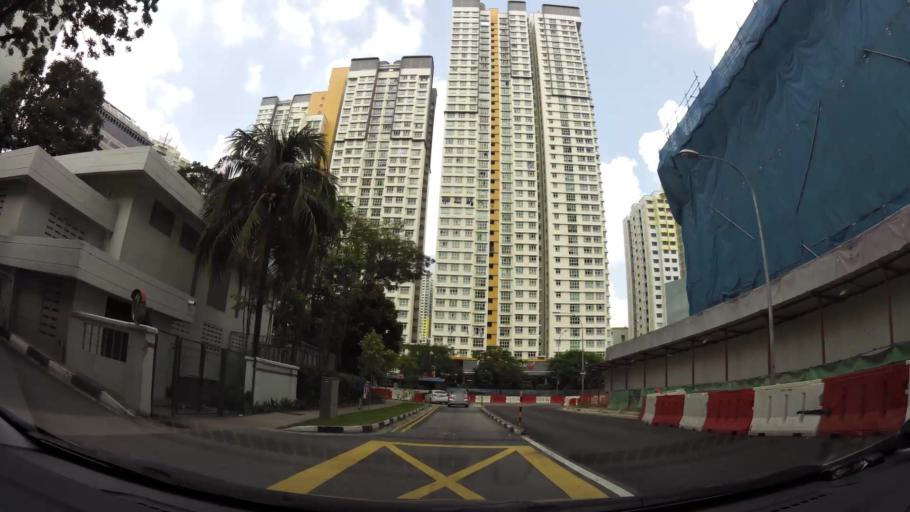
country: SG
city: Singapore
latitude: 1.2852
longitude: 103.8295
